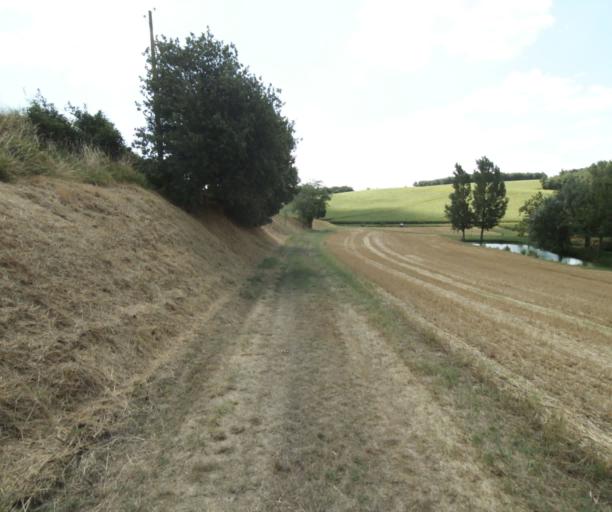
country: FR
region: Midi-Pyrenees
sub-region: Departement de la Haute-Garonne
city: Auriac-sur-Vendinelle
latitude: 43.4598
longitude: 1.7956
